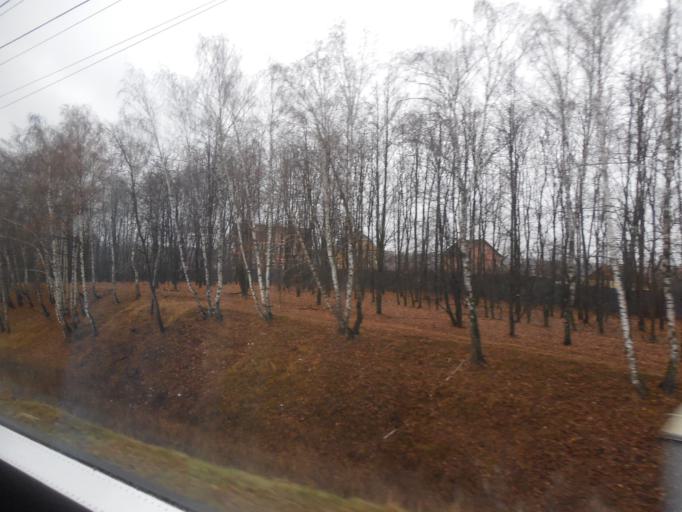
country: RU
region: Moscow
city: Zagor'ye
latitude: 55.5558
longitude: 37.6758
